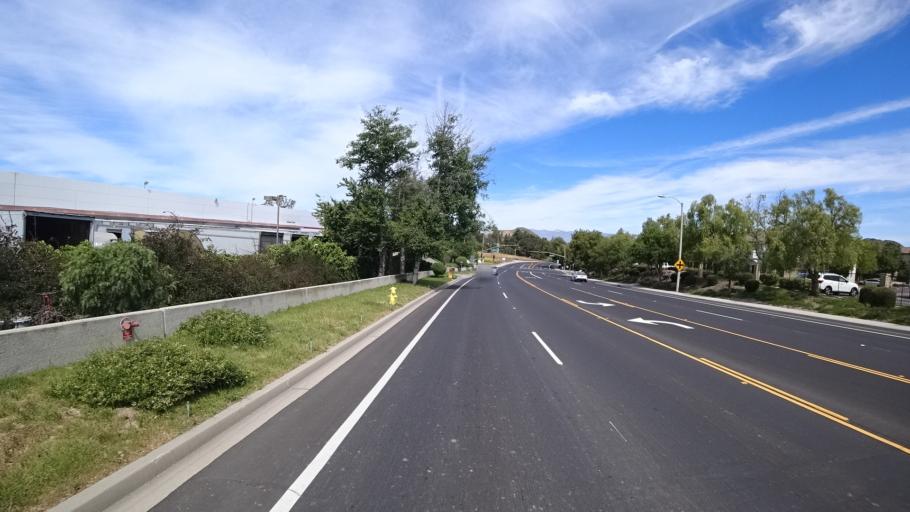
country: US
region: California
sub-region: Ventura County
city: Casa Conejo
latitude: 34.1990
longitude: -118.9233
